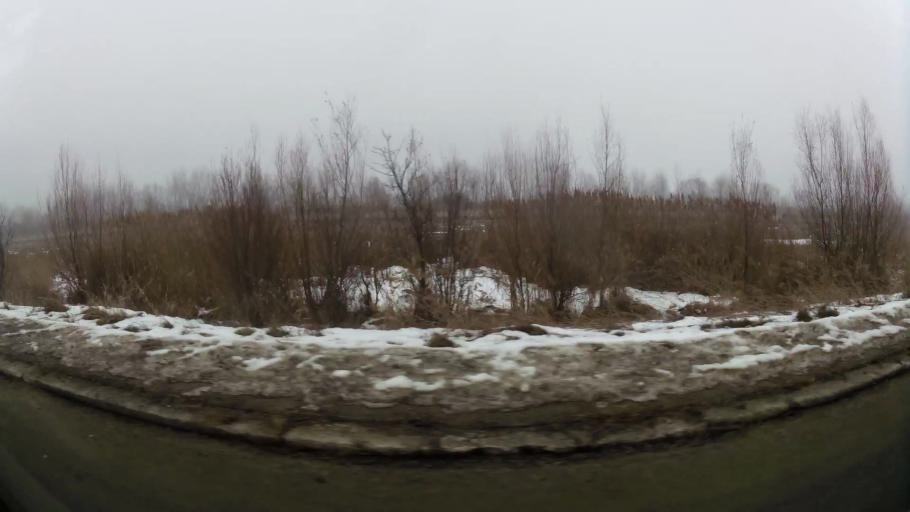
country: RO
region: Ilfov
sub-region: Comuna Chiajna
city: Chiajna
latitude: 44.4661
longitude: 25.9835
